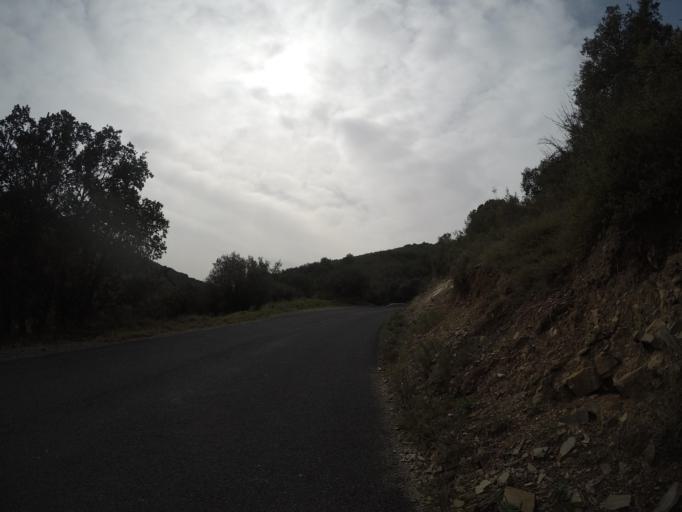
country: FR
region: Languedoc-Roussillon
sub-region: Departement des Pyrenees-Orientales
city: Estagel
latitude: 42.7441
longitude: 2.7253
